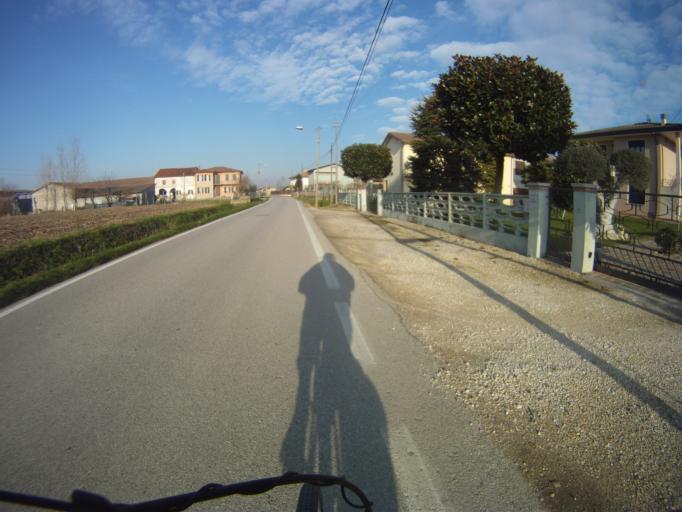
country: IT
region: Veneto
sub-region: Provincia di Padova
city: Polverara
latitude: 45.2973
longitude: 11.9598
